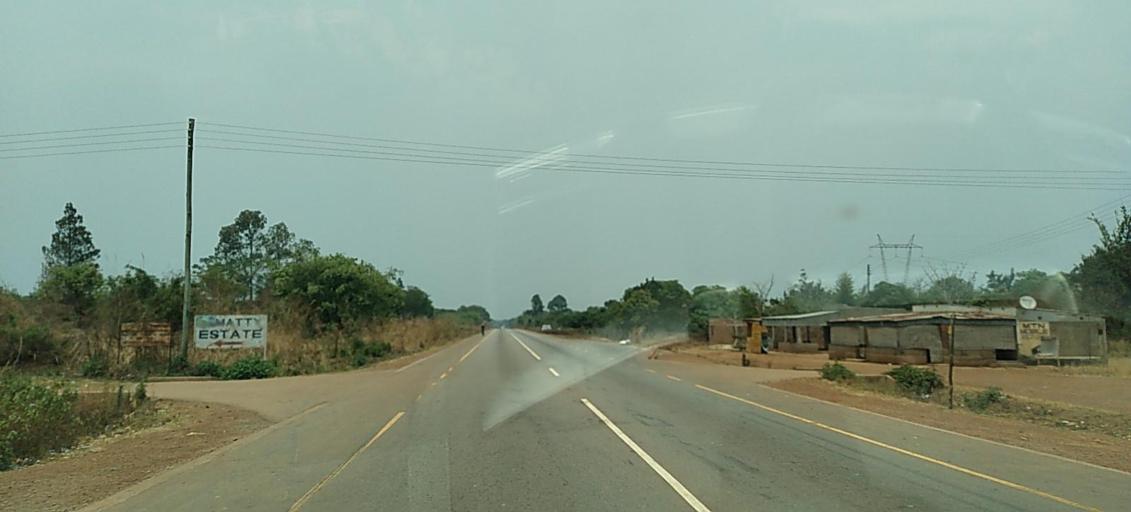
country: ZM
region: Copperbelt
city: Chingola
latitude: -12.5481
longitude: 27.6311
